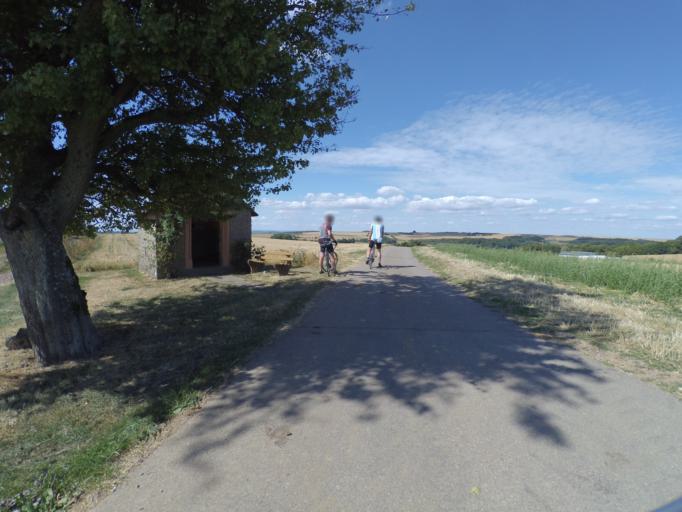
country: DE
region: Rheinland-Pfalz
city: Merzkirchen
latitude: 49.5951
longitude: 6.4965
